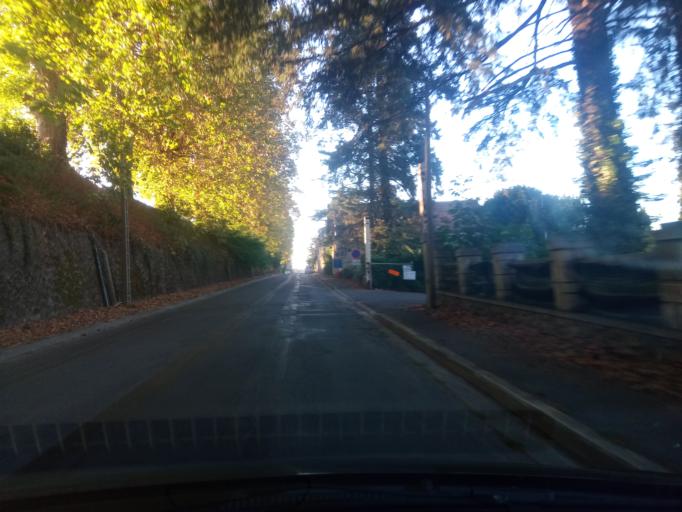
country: FR
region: Poitou-Charentes
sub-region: Departement de la Vienne
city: Montmorillon
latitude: 46.4168
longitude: 0.8755
